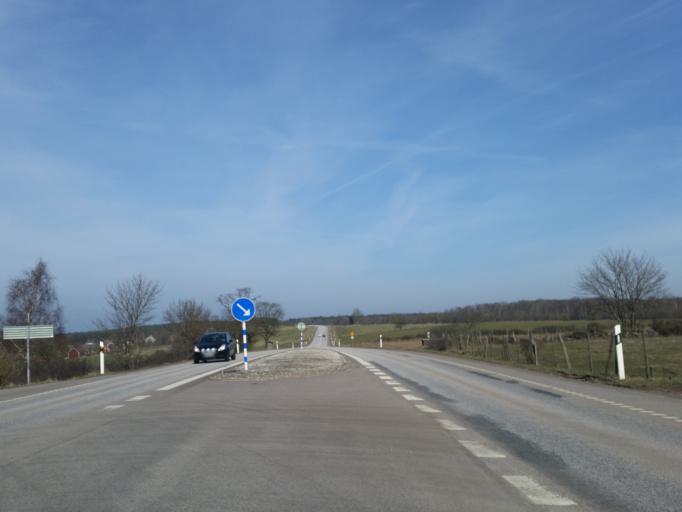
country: SE
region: Kalmar
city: Faerjestaden
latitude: 56.7309
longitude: 16.5410
